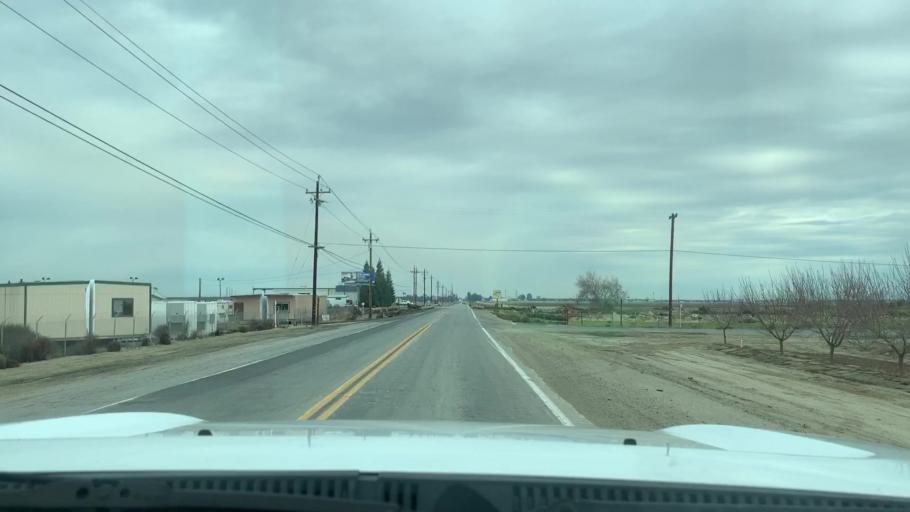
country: US
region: California
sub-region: Kern County
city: Rosedale
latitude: 35.3678
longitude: -119.2521
